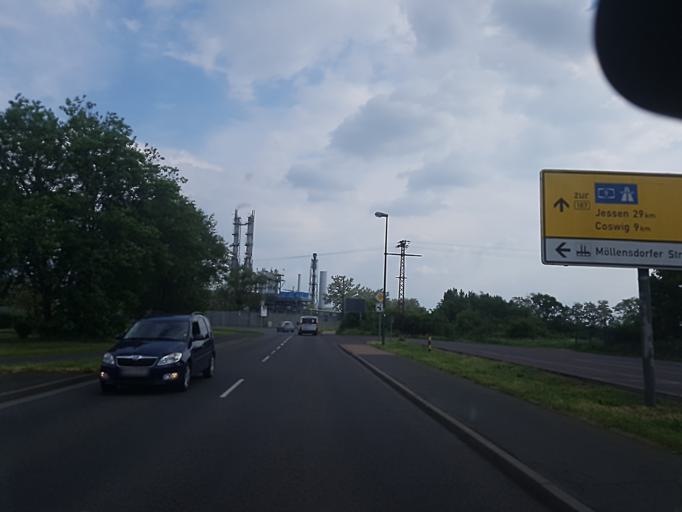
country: DE
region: Saxony-Anhalt
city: Nudersdorf
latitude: 51.8839
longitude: 12.5743
